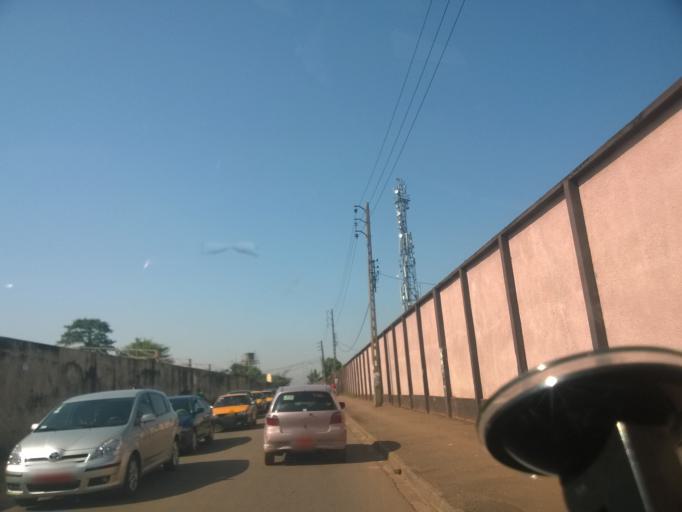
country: CM
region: Centre
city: Yaounde
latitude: 3.8556
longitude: 11.5087
